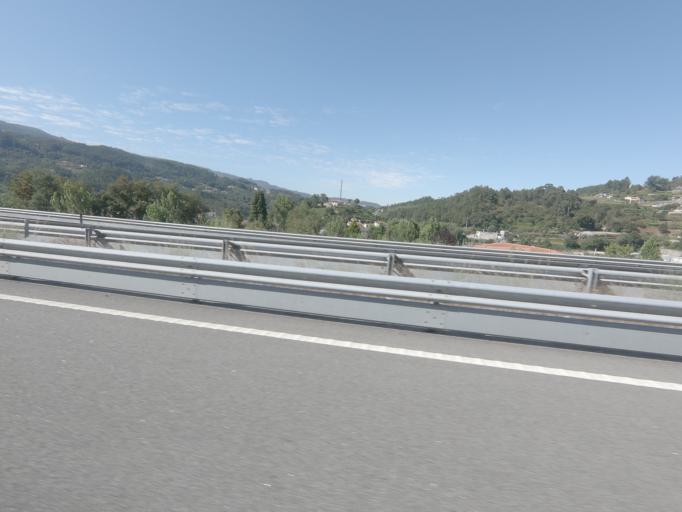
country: PT
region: Porto
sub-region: Amarante
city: Amarante
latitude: 41.2579
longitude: -8.0516
